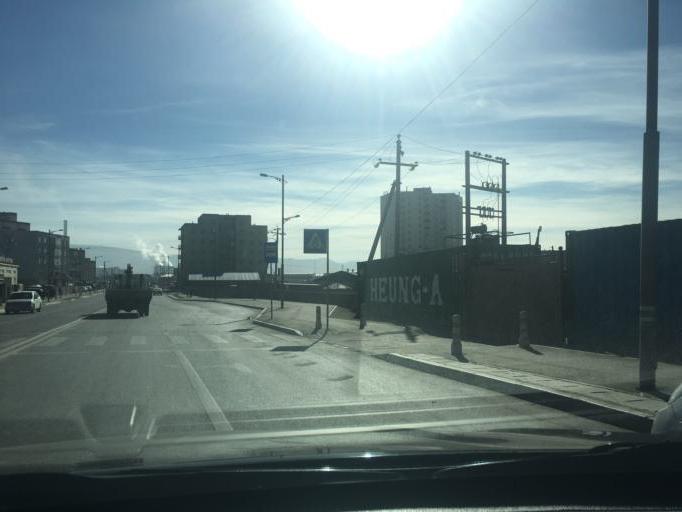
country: MN
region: Ulaanbaatar
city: Ulaanbaatar
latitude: 47.9133
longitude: 106.7821
